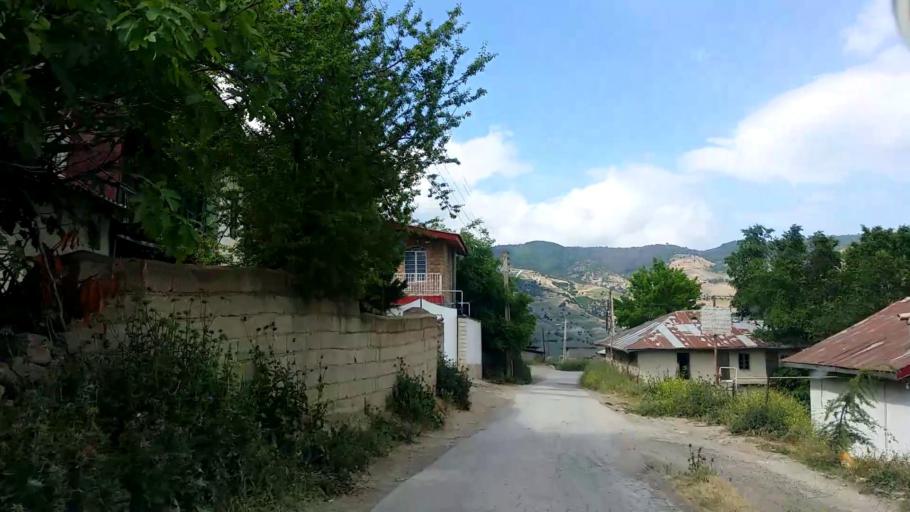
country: IR
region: Mazandaran
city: Chalus
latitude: 36.5358
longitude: 51.2709
